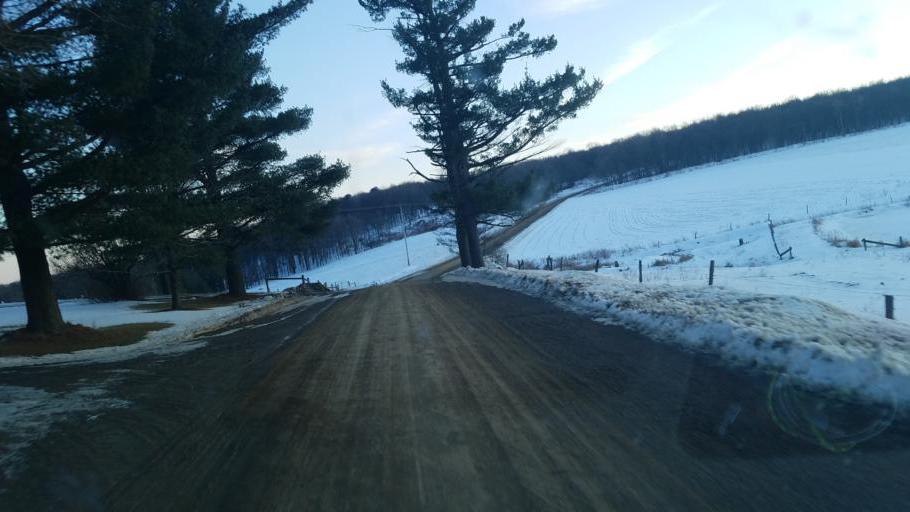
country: US
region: Pennsylvania
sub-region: Tioga County
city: Westfield
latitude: 42.0114
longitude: -77.6826
